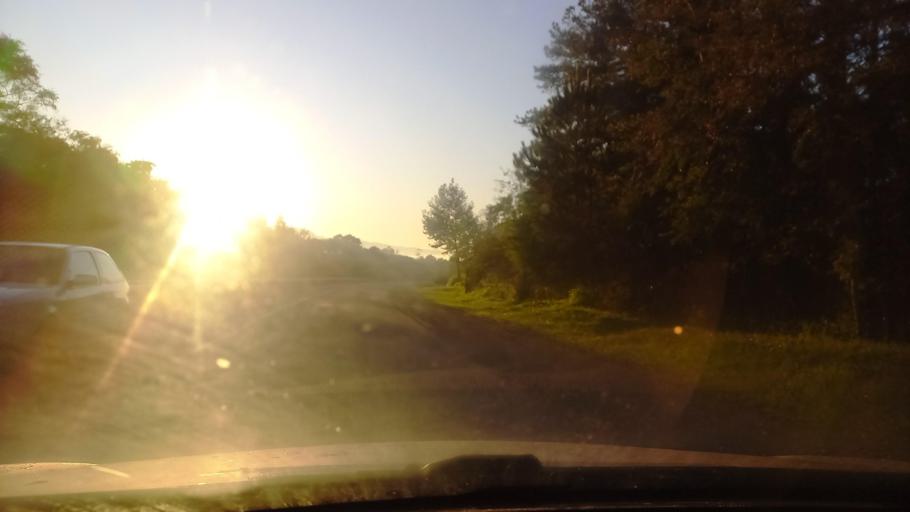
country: BR
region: Rio Grande do Sul
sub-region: Candelaria
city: Candelaria
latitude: -29.6810
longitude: -52.8401
